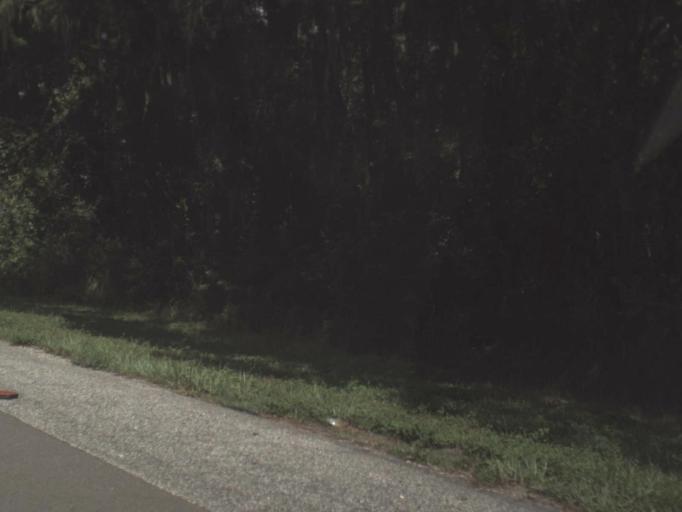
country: US
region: Florida
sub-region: Hillsborough County
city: Balm
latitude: 27.7047
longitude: -82.1856
